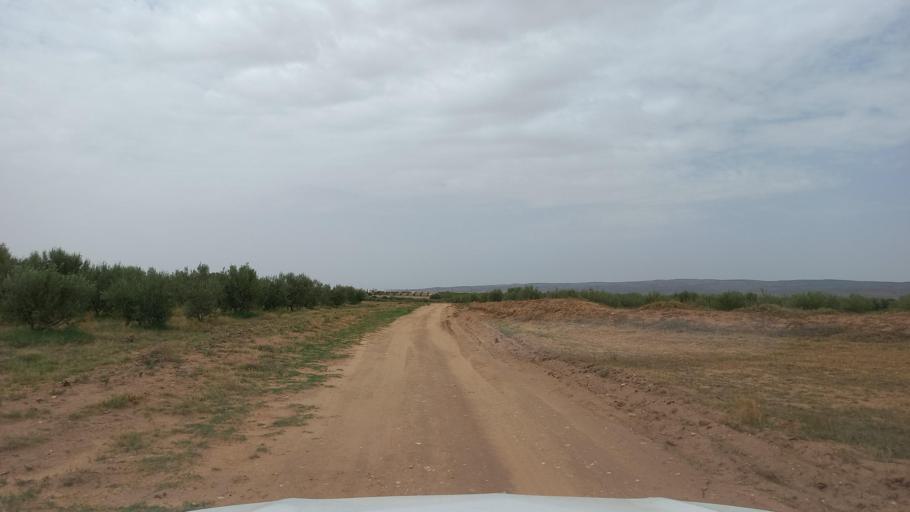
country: TN
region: Al Qasrayn
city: Kasserine
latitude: 35.2867
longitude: 9.0218
